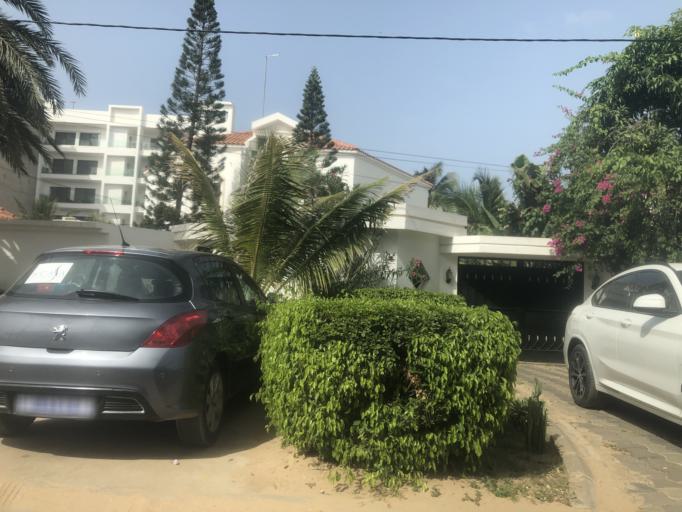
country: SN
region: Dakar
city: Mermoz Boabab
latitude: 14.7384
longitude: -17.5128
